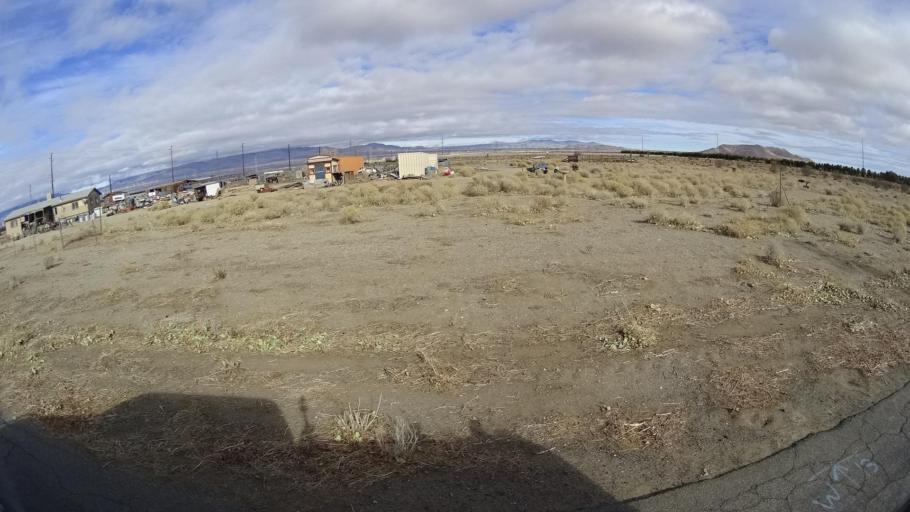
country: US
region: California
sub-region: Kern County
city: Rosamond
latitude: 34.8340
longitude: -118.3244
